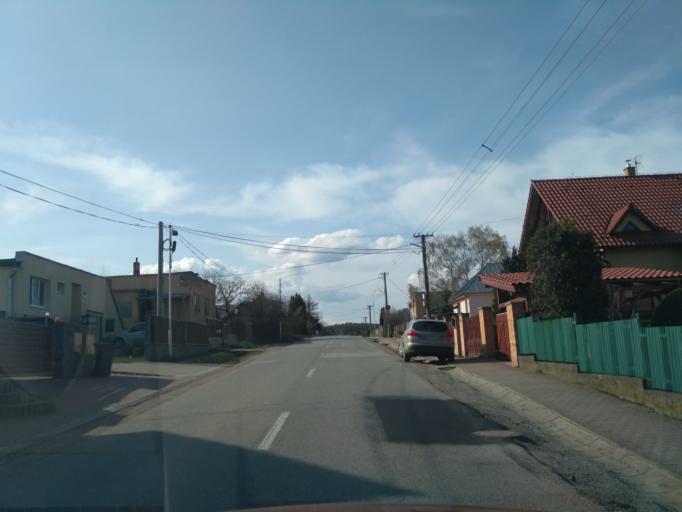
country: SK
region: Kosicky
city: Kosice
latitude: 48.6874
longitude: 21.2141
